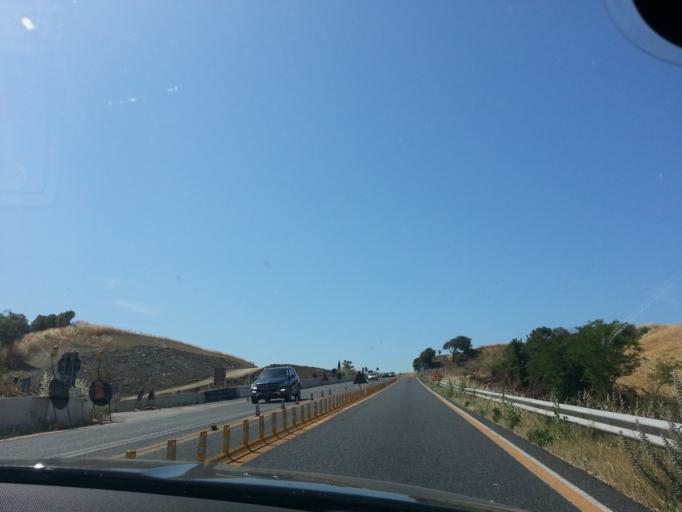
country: IT
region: Latium
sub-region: Citta metropolitana di Roma Capitale
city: Aurelia
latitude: 42.1893
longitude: 11.7863
